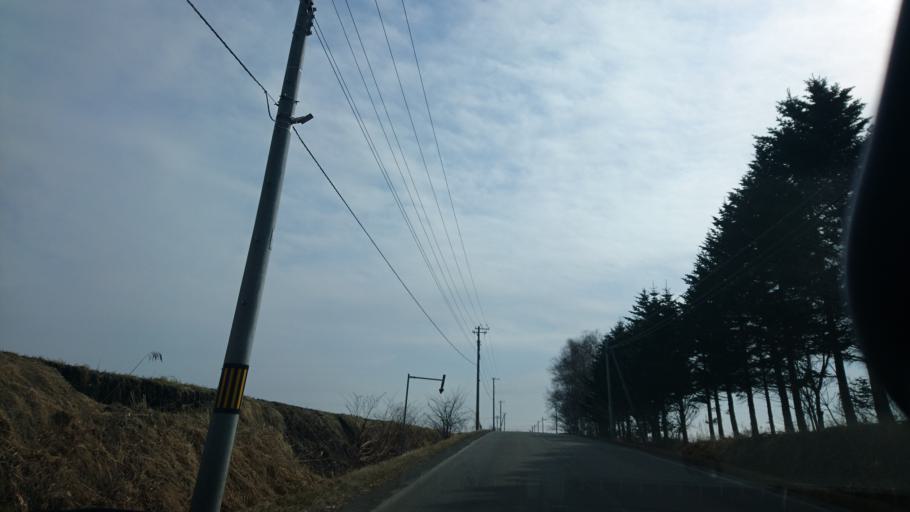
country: JP
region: Hokkaido
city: Otofuke
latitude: 42.9935
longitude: 143.2201
